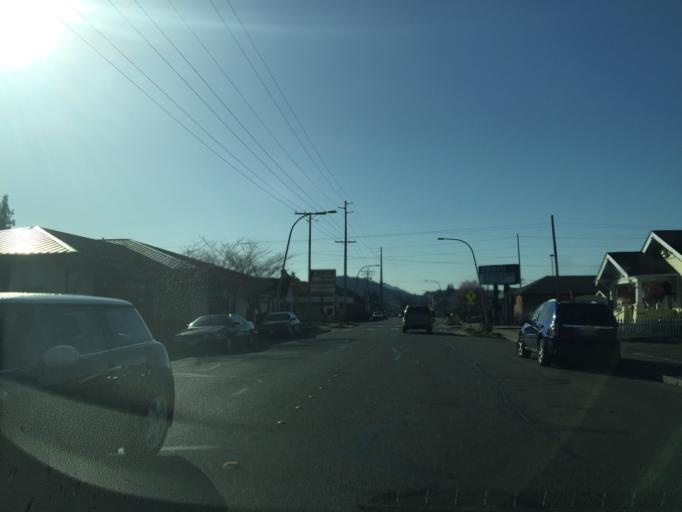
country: US
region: Washington
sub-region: Whatcom County
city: Bellingham
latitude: 48.7661
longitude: -122.4860
